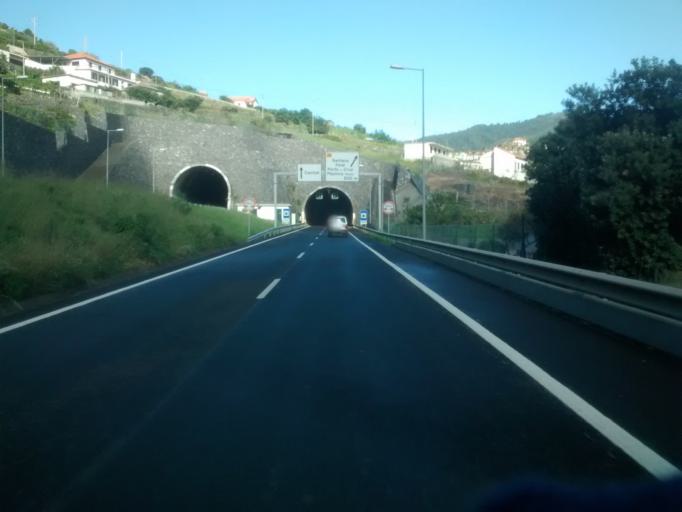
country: PT
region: Madeira
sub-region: Machico
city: Machico
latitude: 32.7217
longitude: -16.7753
